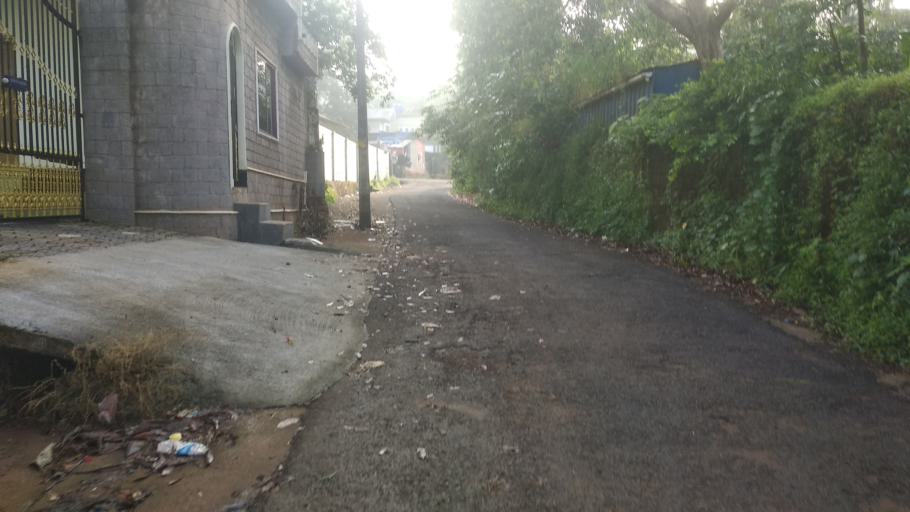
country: IN
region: Kerala
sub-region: Malappuram
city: Malappuram
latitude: 10.9920
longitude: 76.0467
